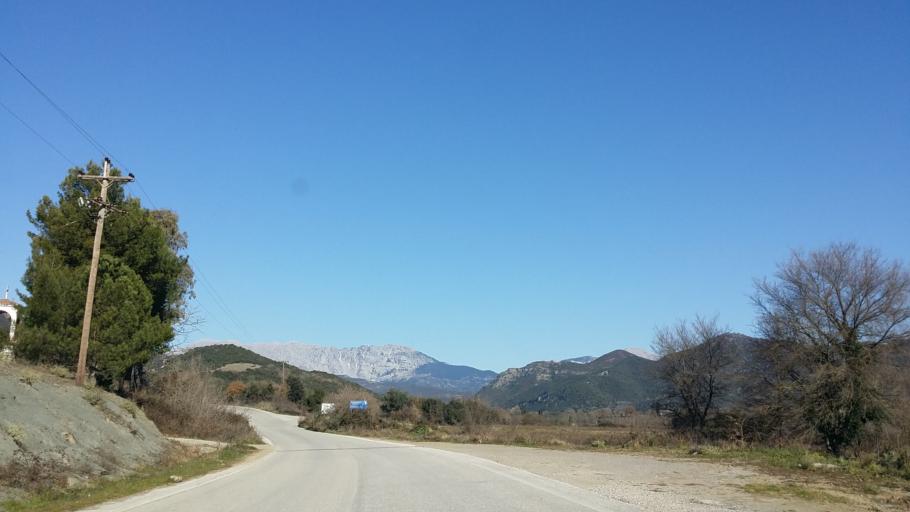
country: GR
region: West Greece
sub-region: Nomos Aitolias kai Akarnanias
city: Sardinia
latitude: 38.8722
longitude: 21.3404
